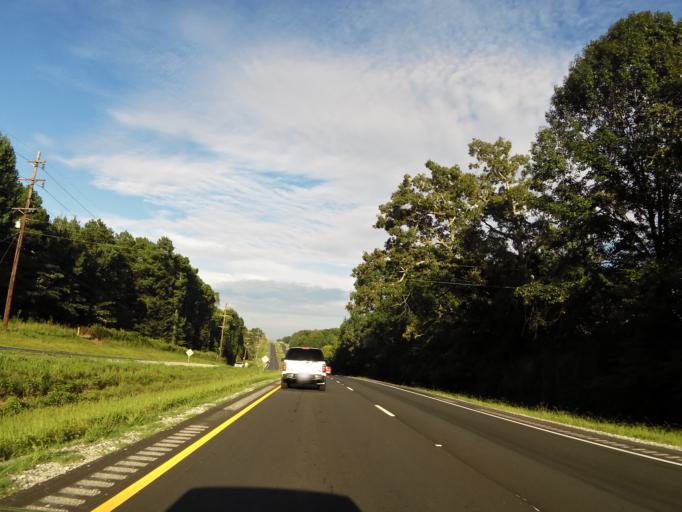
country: US
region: Alabama
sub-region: Lauderdale County
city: Killen
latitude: 34.8594
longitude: -87.4898
